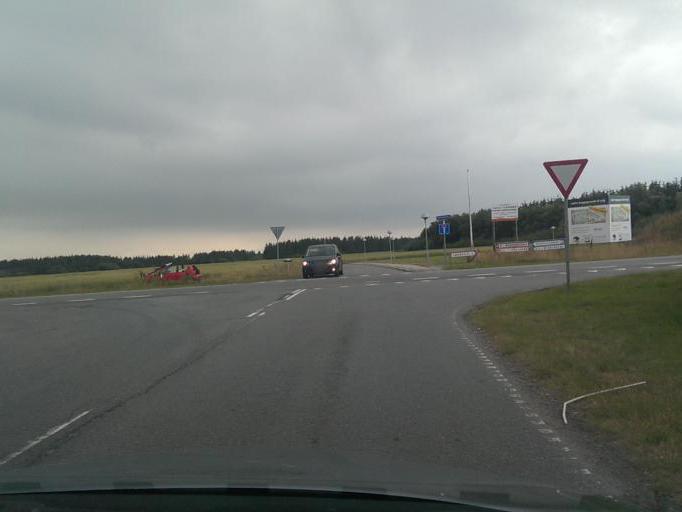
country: DK
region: North Denmark
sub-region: Jammerbugt Kommune
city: Pandrup
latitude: 57.3654
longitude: 9.7299
